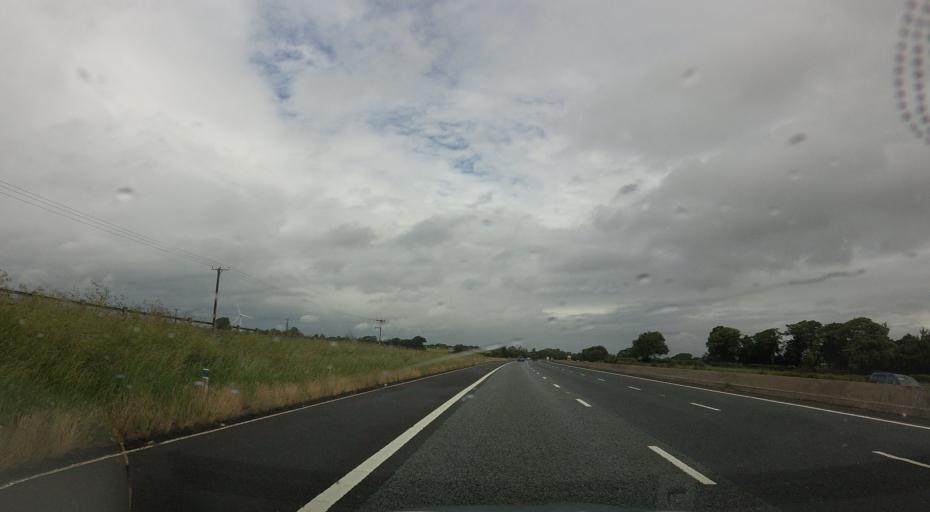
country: GB
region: England
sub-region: Cumbria
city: Scotby
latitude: 54.8179
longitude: -2.8859
